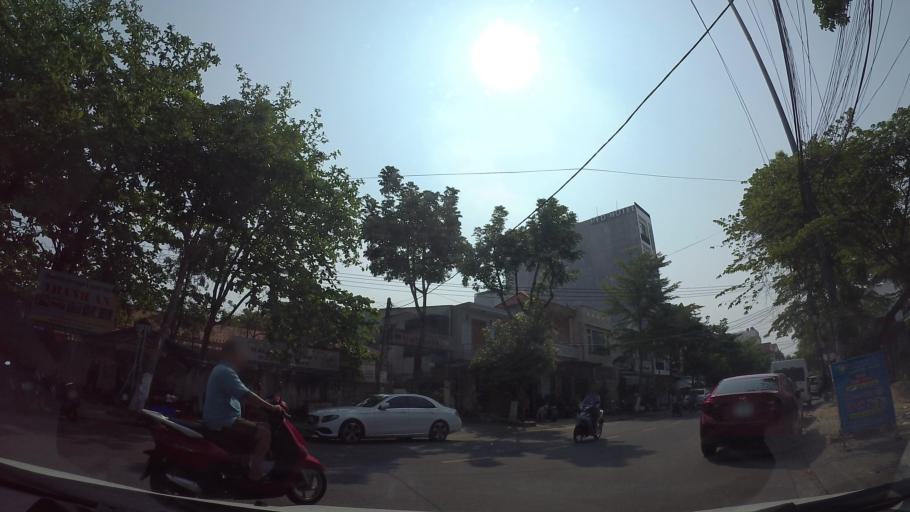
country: VN
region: Da Nang
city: Son Tra
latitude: 16.0418
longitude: 108.2437
